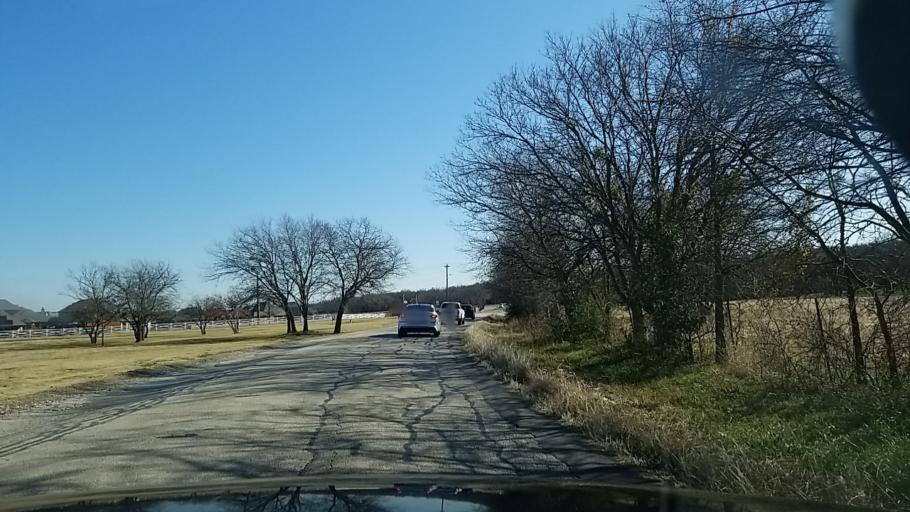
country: US
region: Texas
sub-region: Denton County
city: Argyle
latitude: 33.1308
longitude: -97.1956
